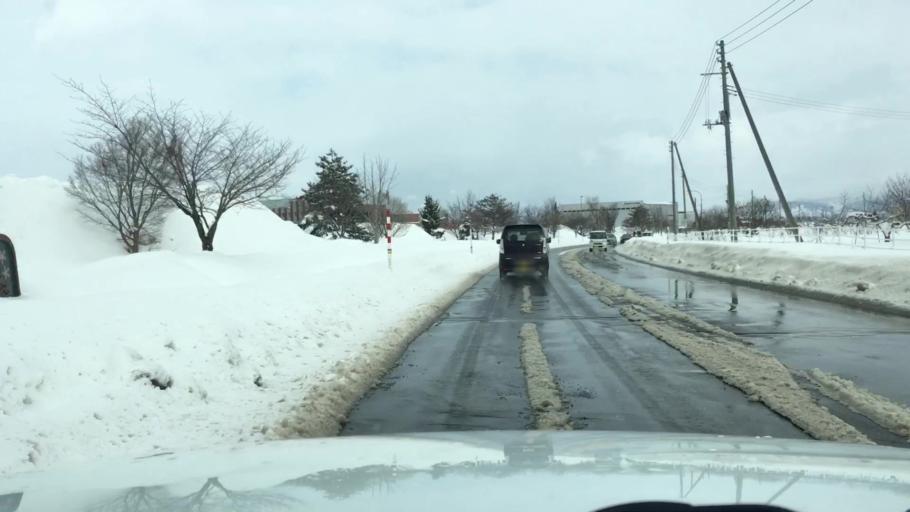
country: JP
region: Aomori
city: Hirosaki
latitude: 40.5846
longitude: 140.5006
